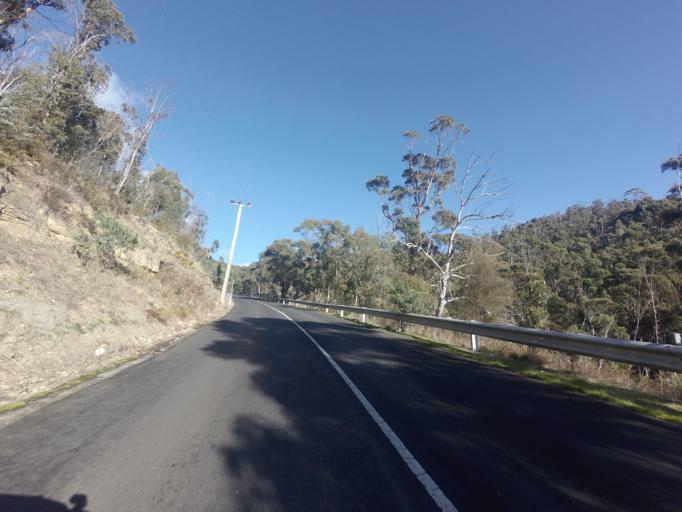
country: AU
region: Tasmania
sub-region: Glenorchy
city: Berriedale
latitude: -42.8212
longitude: 147.2117
